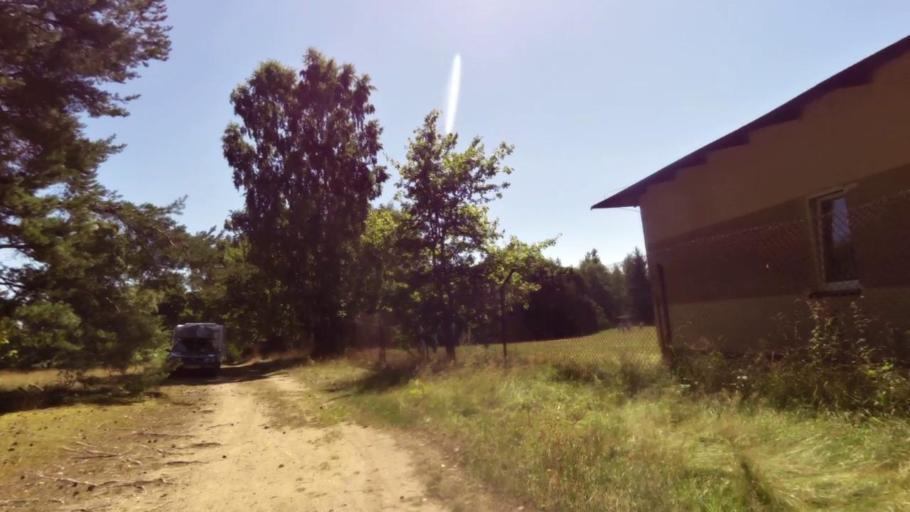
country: PL
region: West Pomeranian Voivodeship
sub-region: Powiat szczecinecki
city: Bialy Bor
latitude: 53.8554
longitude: 16.8679
